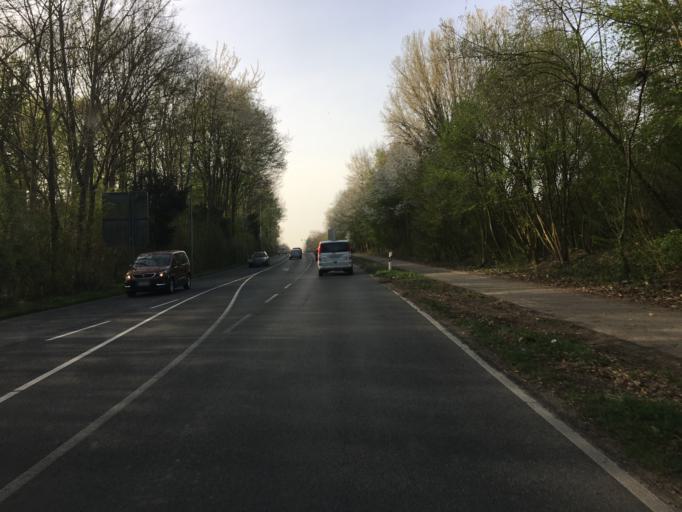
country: DE
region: North Rhine-Westphalia
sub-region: Regierungsbezirk Koln
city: Hurth
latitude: 50.8816
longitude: 6.8655
